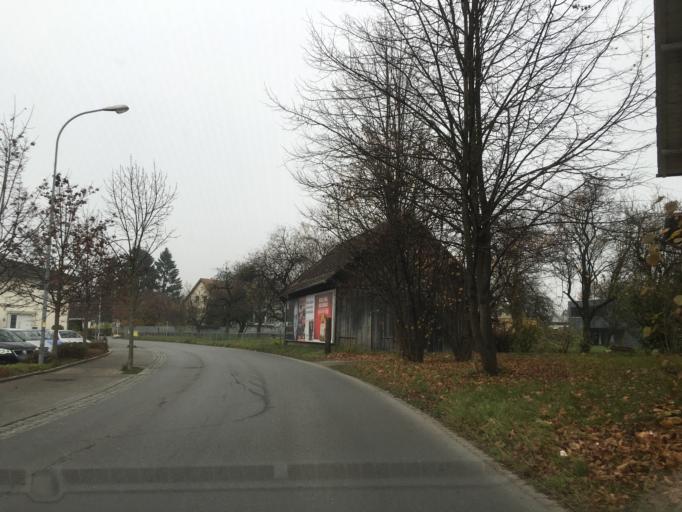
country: AT
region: Vorarlberg
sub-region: Politischer Bezirk Dornbirn
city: Lustenau
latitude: 47.4309
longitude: 9.6708
